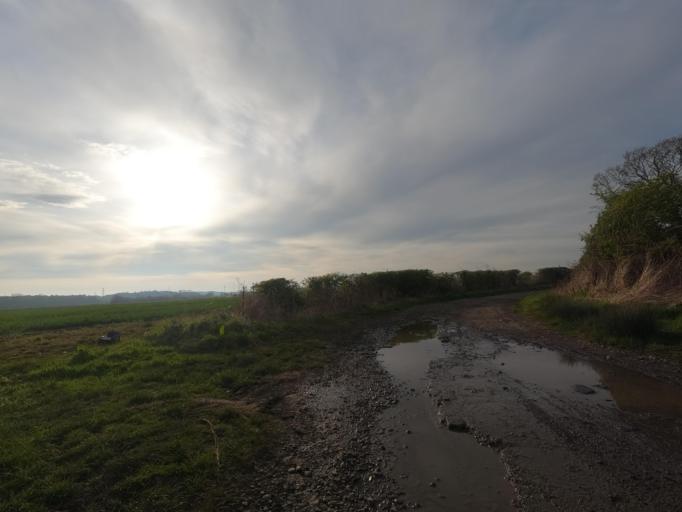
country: GB
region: England
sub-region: Northumberland
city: Cramlington
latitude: 55.0809
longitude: -1.6089
